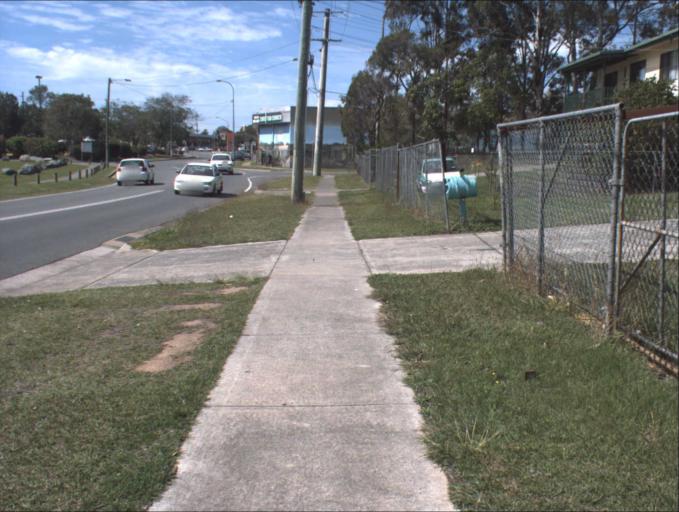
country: AU
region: Queensland
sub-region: Logan
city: Waterford West
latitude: -27.6787
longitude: 153.1137
